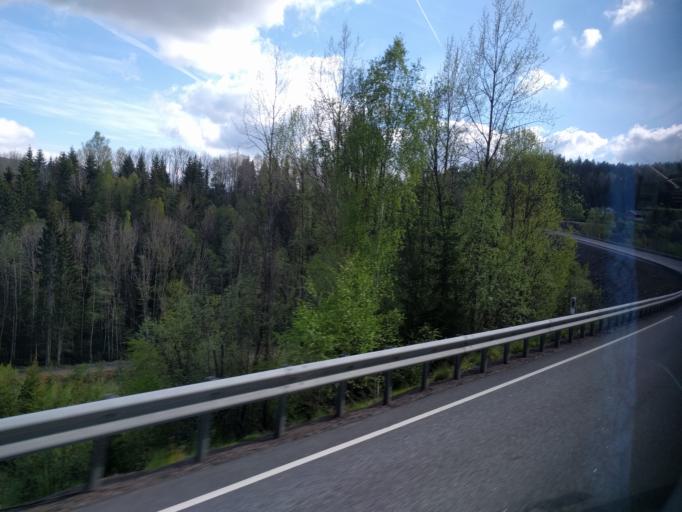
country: NO
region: Vestfold
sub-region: Lardal
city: Svarstad
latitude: 59.3754
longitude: 9.9318
